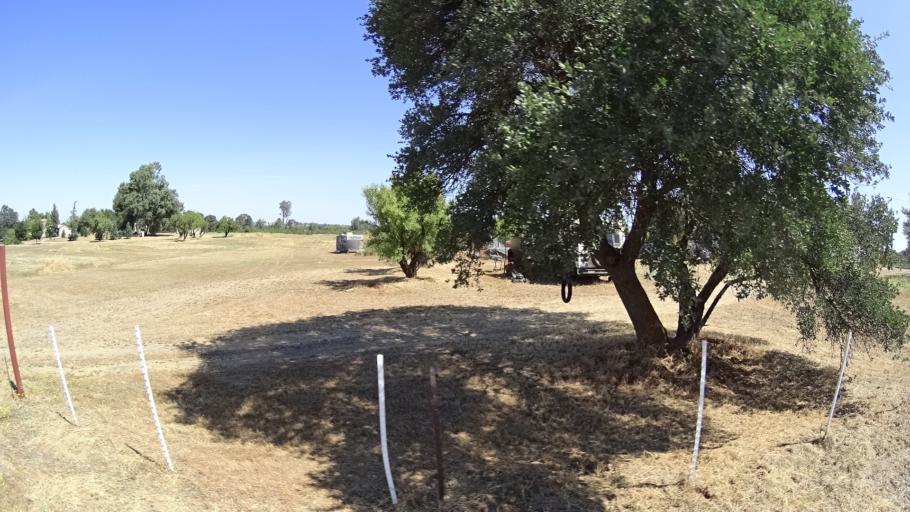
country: US
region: California
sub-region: Calaveras County
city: Rancho Calaveras
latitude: 38.1633
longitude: -120.9140
